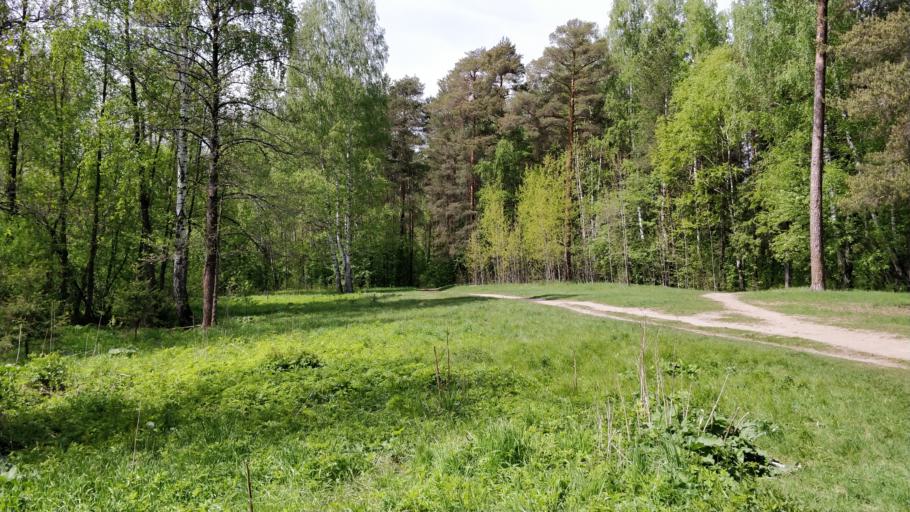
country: RU
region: Perm
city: Kondratovo
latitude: 57.9883
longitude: 56.1445
